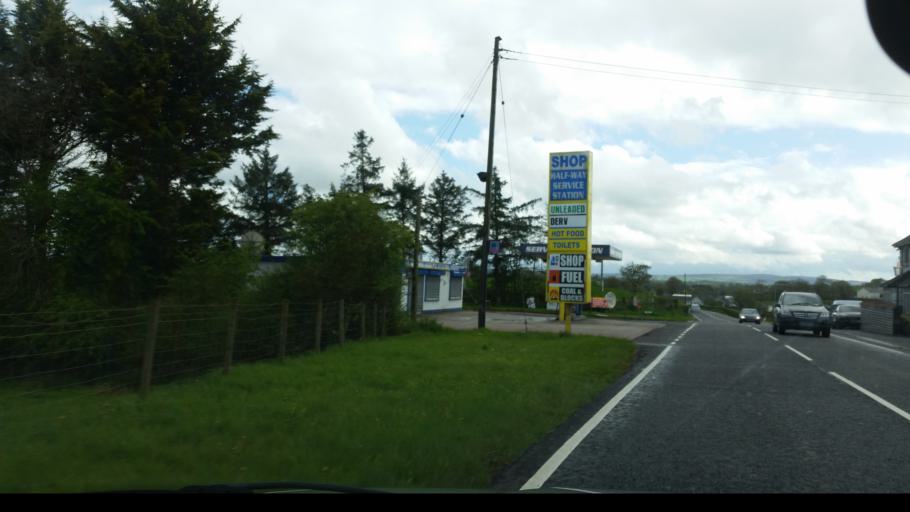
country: GB
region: Northern Ireland
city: Fintona
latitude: 54.5424
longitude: -7.2900
